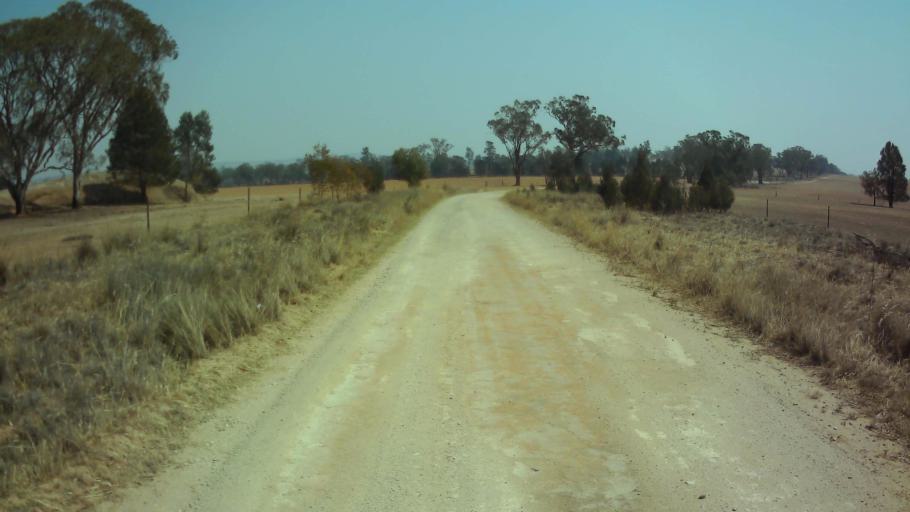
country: AU
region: New South Wales
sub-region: Weddin
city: Grenfell
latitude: -33.6502
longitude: 148.2704
